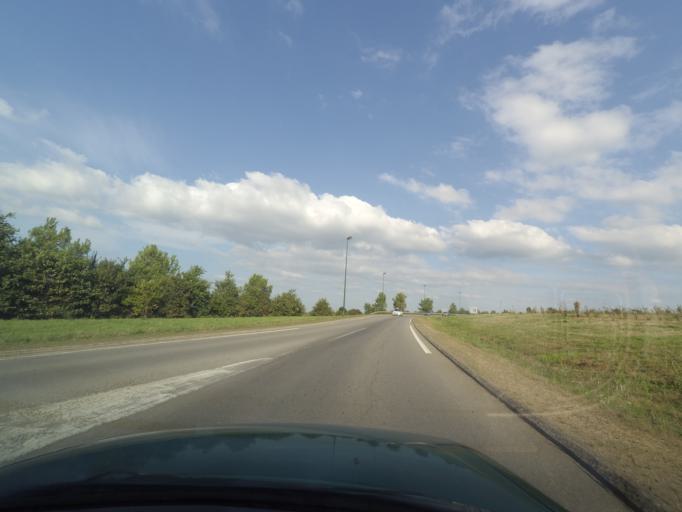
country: FR
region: Pays de la Loire
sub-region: Departement de la Loire-Atlantique
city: Saint-Philbert-de-Grand-Lieu
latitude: 47.0340
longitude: -1.6602
